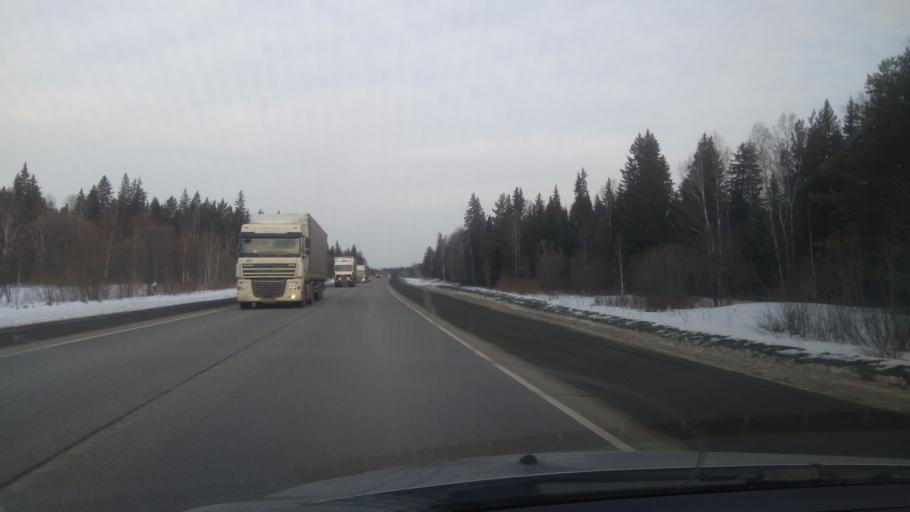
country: RU
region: Sverdlovsk
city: Atig
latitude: 56.8049
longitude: 59.3739
